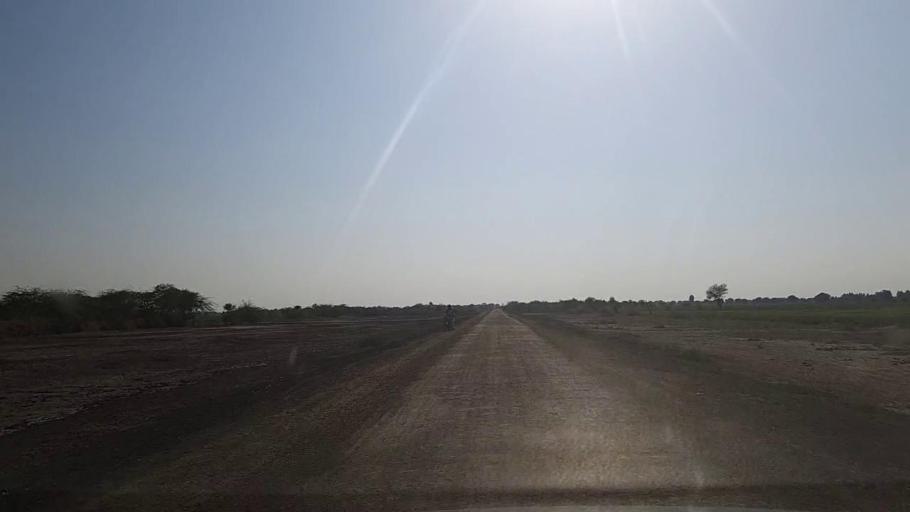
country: PK
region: Sindh
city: Digri
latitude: 25.0405
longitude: 69.2259
